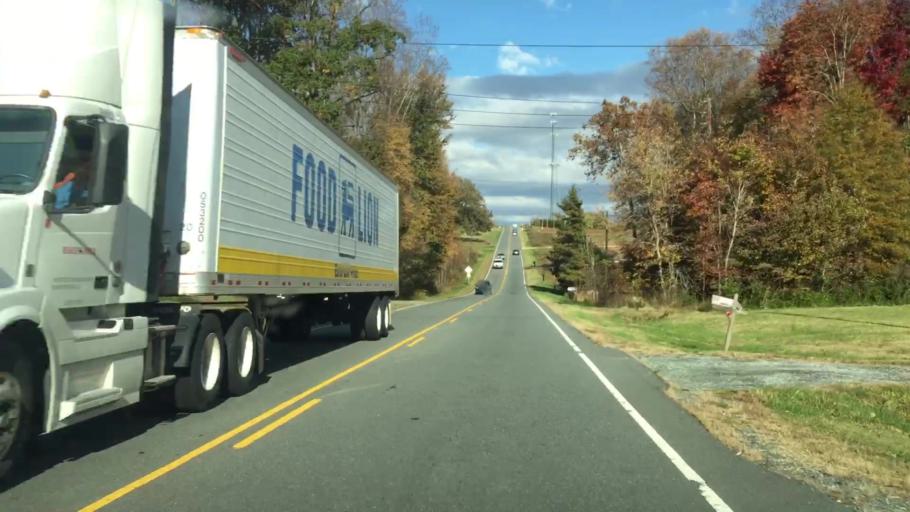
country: US
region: North Carolina
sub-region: Guilford County
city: Oak Ridge
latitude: 36.2135
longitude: -80.0644
